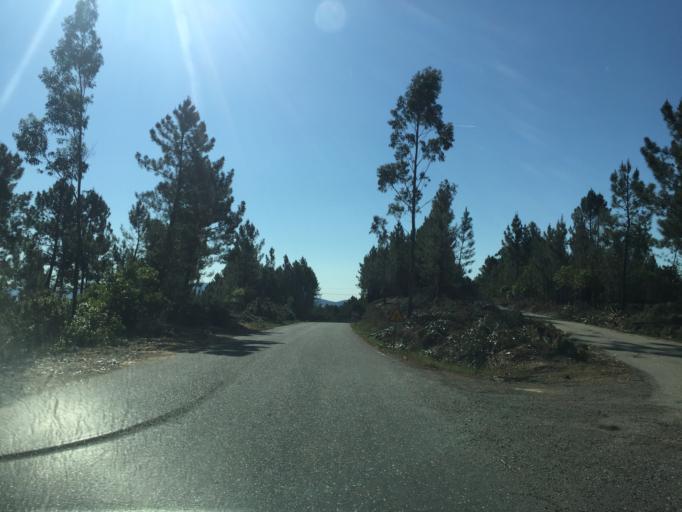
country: PT
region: Coimbra
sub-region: Pampilhosa da Serra
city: Pampilhosa da Serra
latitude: 40.0541
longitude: -7.8483
